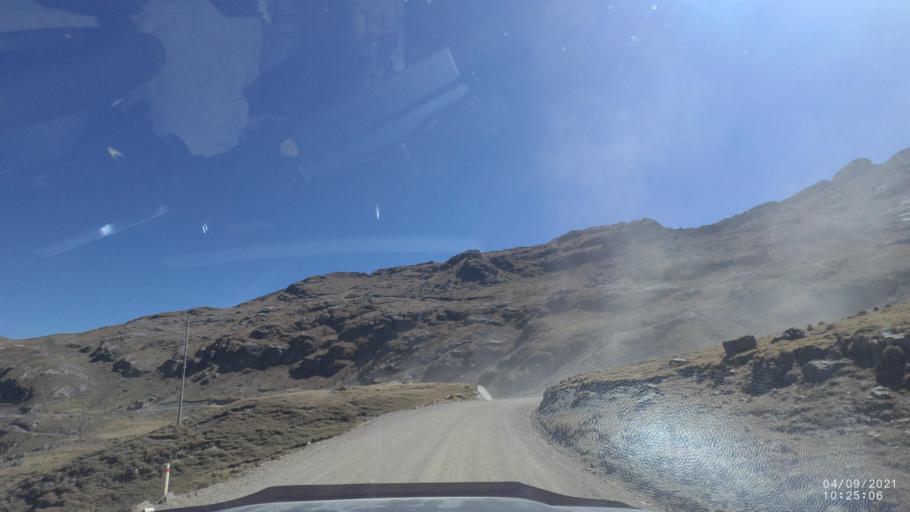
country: BO
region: Cochabamba
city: Sipe Sipe
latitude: -17.3063
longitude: -66.4370
